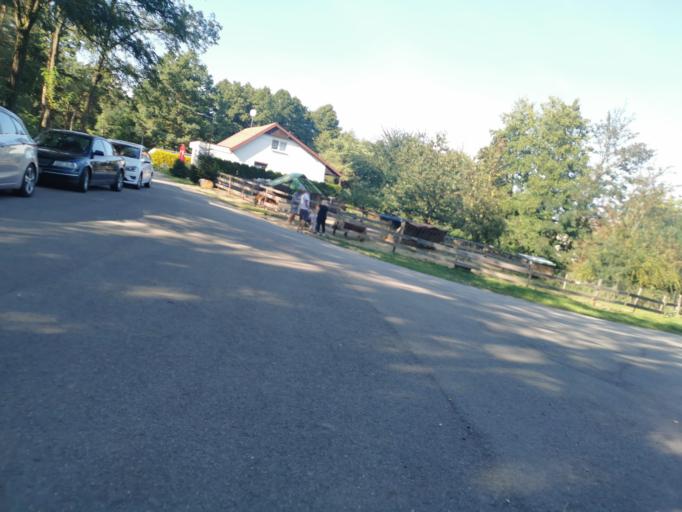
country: SK
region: Trnavsky
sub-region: Okres Senica
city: Senica
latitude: 48.6457
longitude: 17.2687
